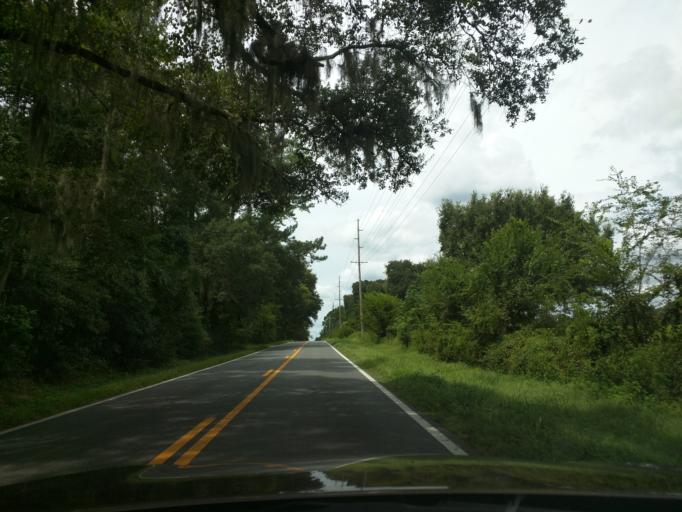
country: US
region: Florida
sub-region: Leon County
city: Tallahassee
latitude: 30.5364
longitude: -84.1507
